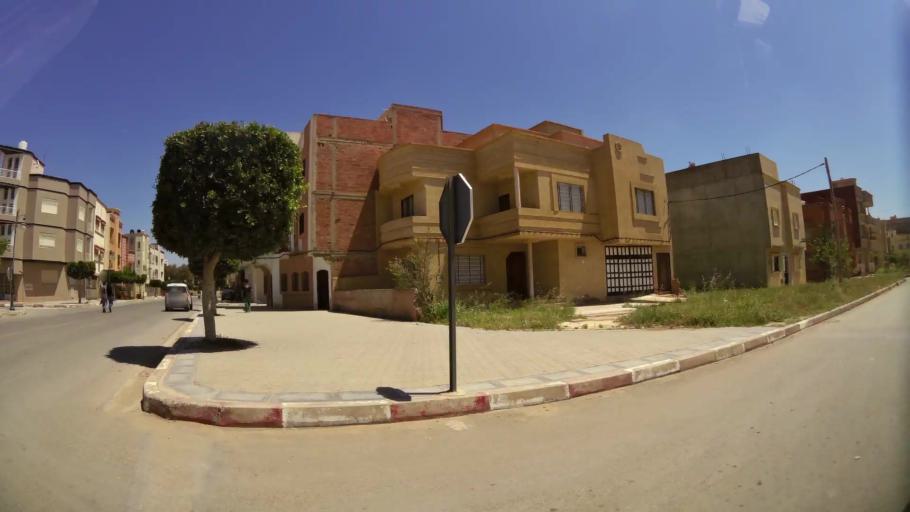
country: MA
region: Oriental
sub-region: Berkane-Taourirt
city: Madagh
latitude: 35.0792
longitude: -2.2288
